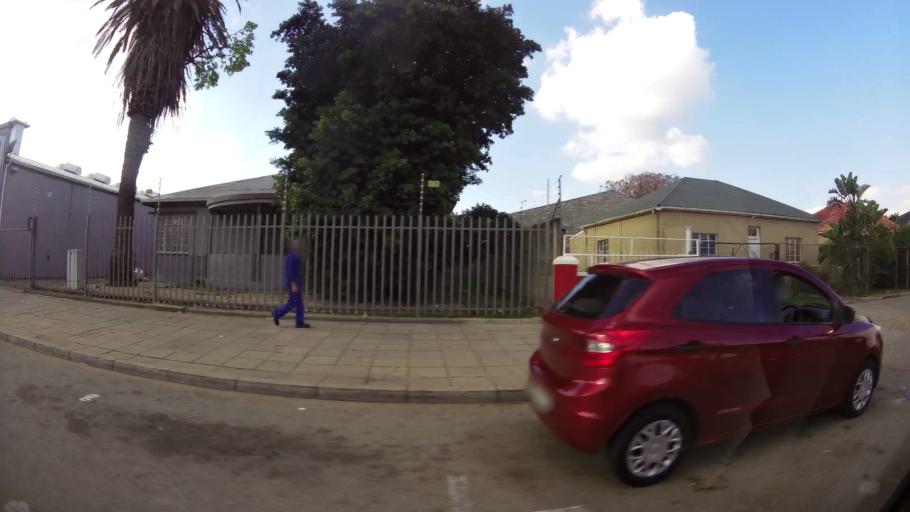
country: ZA
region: Eastern Cape
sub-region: Nelson Mandela Bay Metropolitan Municipality
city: Uitenhage
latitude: -33.7673
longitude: 25.3928
